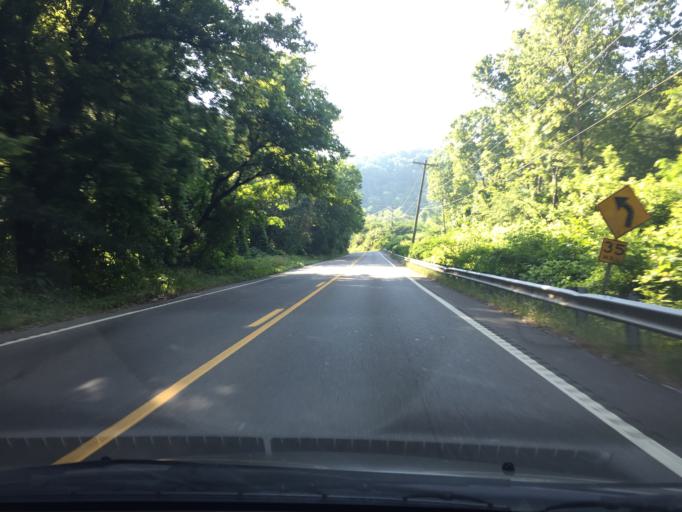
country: US
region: Tennessee
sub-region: Hamilton County
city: Collegedale
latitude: 35.0775
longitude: -85.0458
